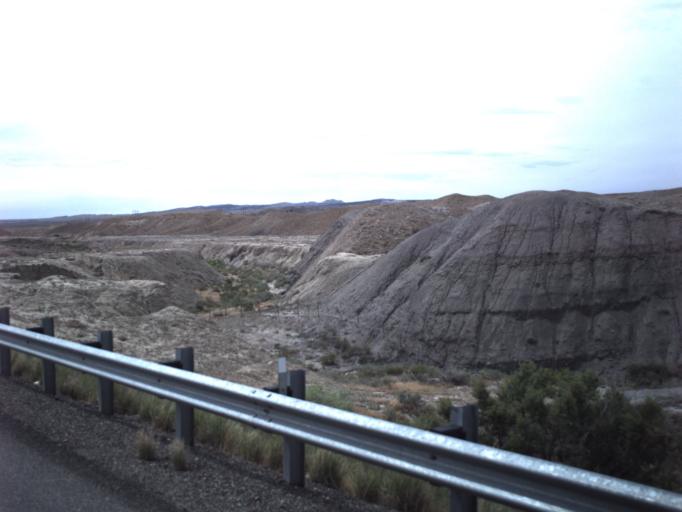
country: US
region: Utah
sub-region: Carbon County
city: East Carbon City
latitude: 39.2892
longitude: -110.3521
